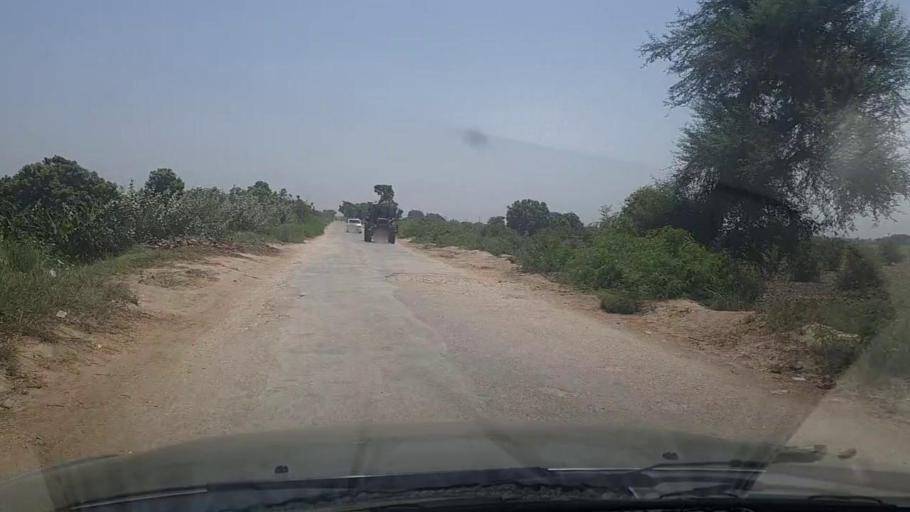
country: PK
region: Sindh
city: Tando Muhammad Khan
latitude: 25.2739
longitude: 68.6260
